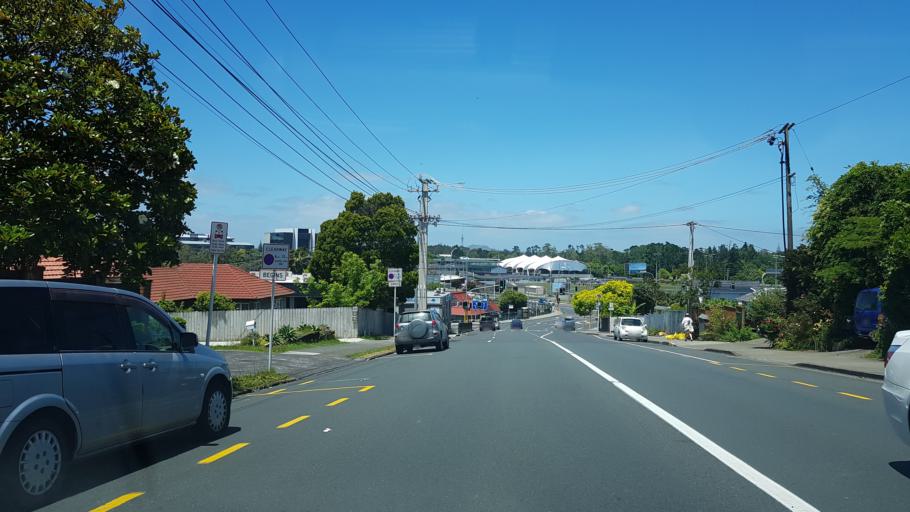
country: NZ
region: Auckland
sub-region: Auckland
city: North Shore
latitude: -36.7783
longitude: 174.7501
